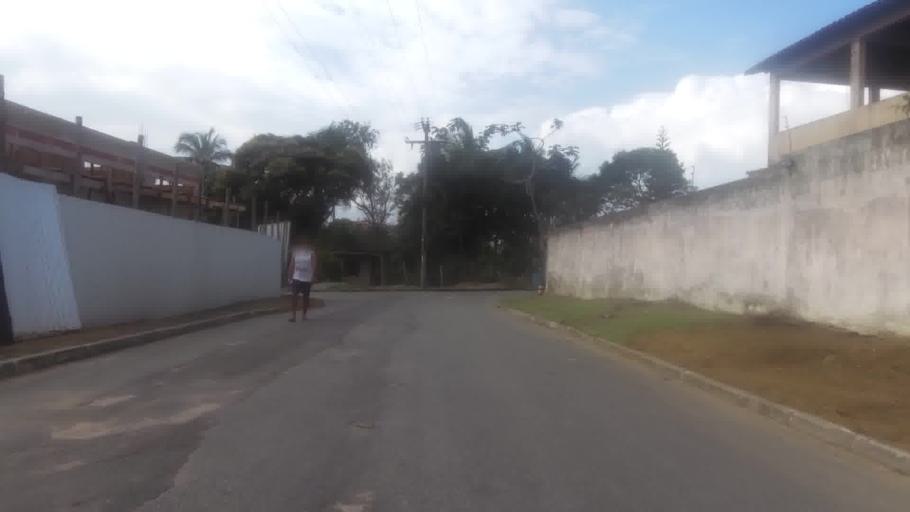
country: BR
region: Espirito Santo
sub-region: Guarapari
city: Guarapari
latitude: -20.7645
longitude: -40.5763
